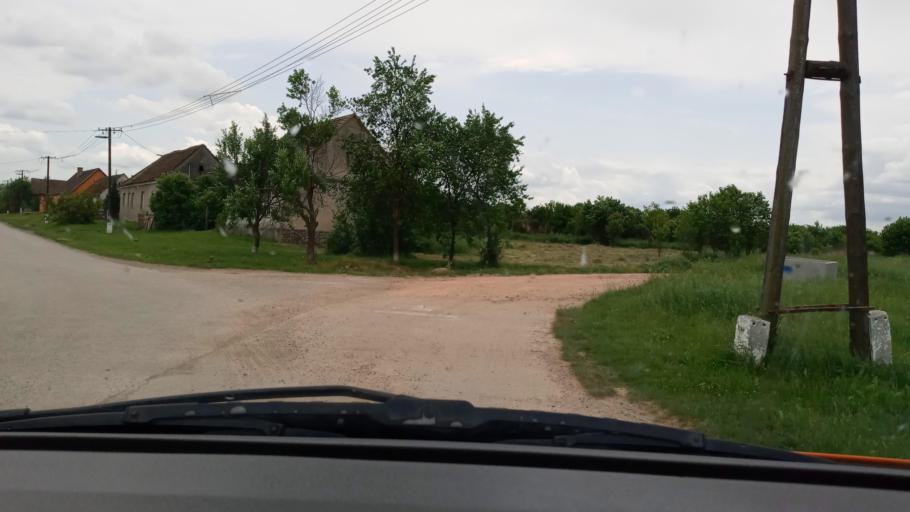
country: HU
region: Baranya
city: Vajszlo
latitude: 45.8218
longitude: 17.9938
